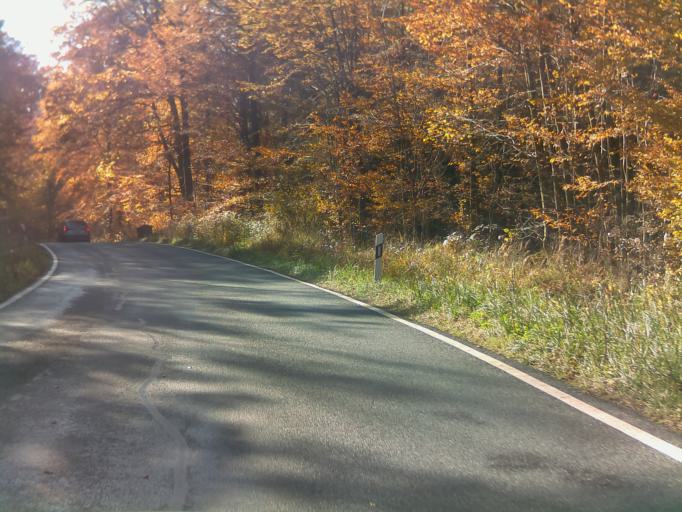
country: DE
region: Bavaria
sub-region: Upper Franconia
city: Burgwindheim
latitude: 49.8636
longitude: 10.5137
